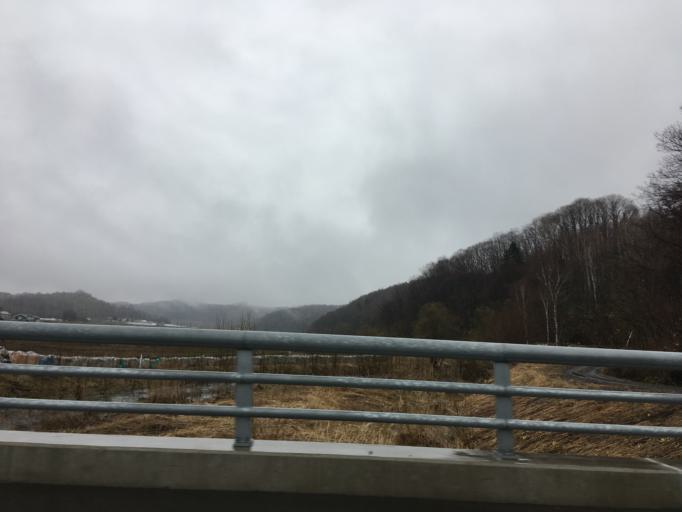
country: JP
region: Hokkaido
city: Nayoro
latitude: 44.0800
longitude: 142.4196
